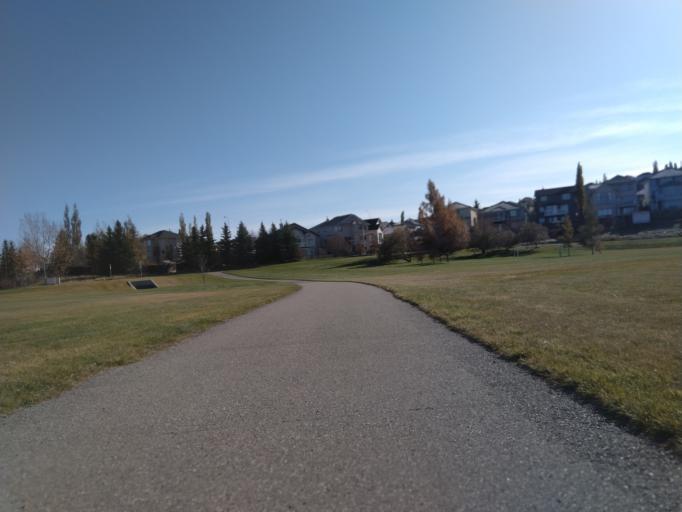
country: CA
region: Alberta
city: Calgary
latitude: 51.1404
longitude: -114.1242
